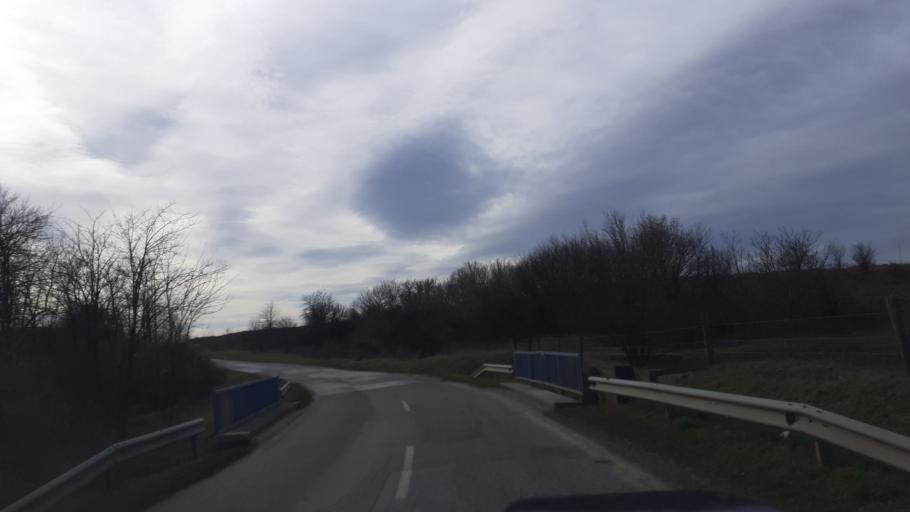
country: HU
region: Fejer
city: Sarbogard
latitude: 46.9106
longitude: 18.6626
